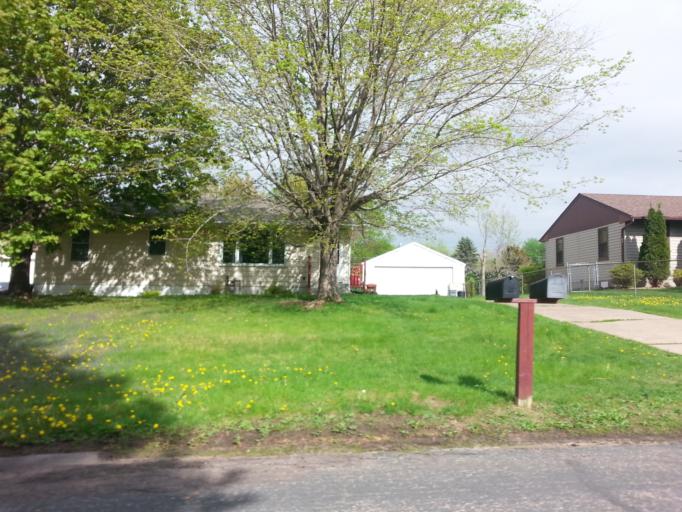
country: US
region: Minnesota
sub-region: Ramsey County
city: Maplewood
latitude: 44.9424
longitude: -92.9903
